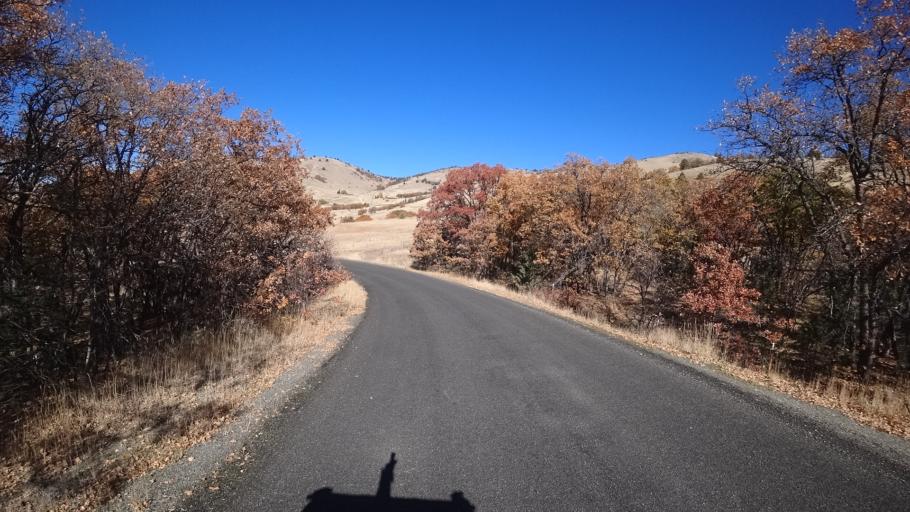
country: US
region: California
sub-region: Siskiyou County
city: Montague
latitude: 41.8300
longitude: -122.3426
